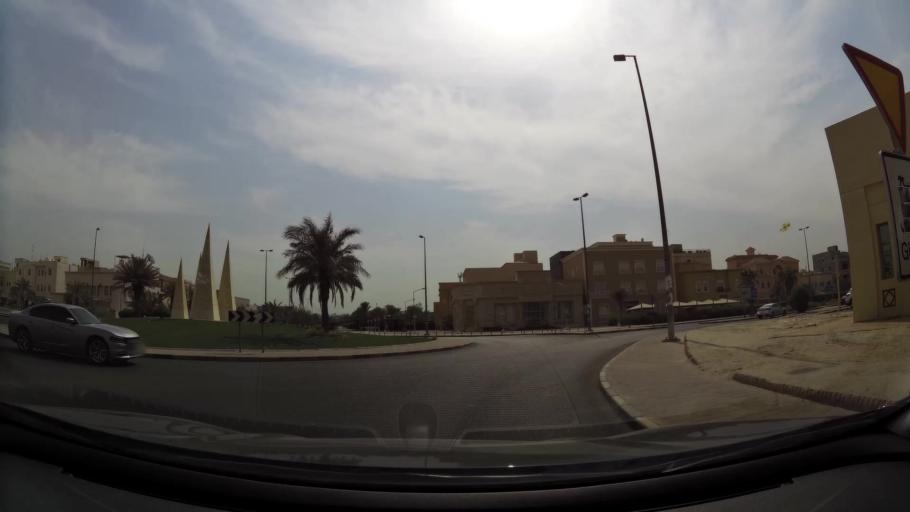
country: KW
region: Al Asimah
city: Ash Shamiyah
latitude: 29.3374
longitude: 47.9812
